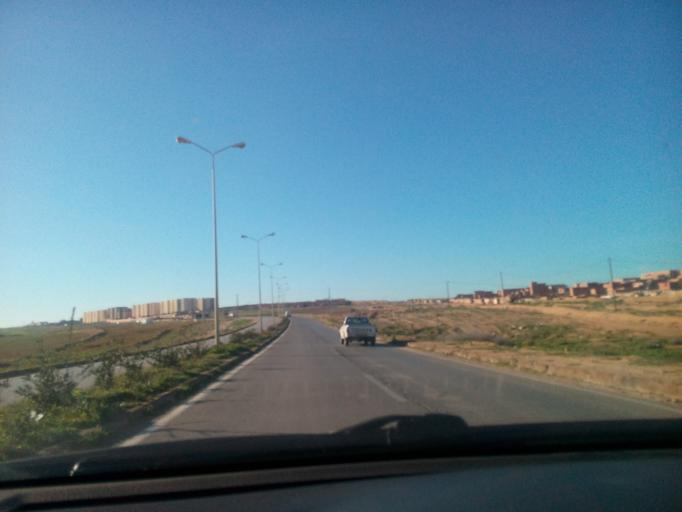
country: DZ
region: Relizane
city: Relizane
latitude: 35.7120
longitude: 0.5250
